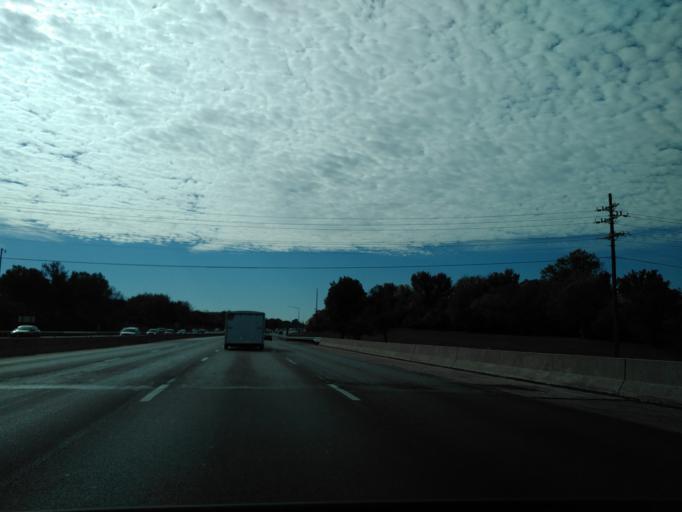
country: US
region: Missouri
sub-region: Saint Louis County
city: Creve Coeur
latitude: 38.6558
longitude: -90.4483
